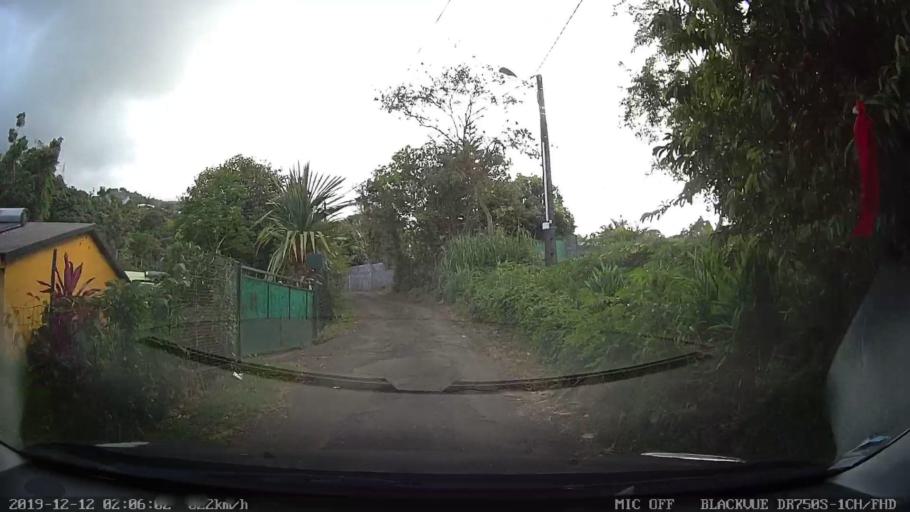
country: RE
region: Reunion
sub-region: Reunion
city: Sainte-Marie
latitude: -20.9348
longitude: 55.5276
